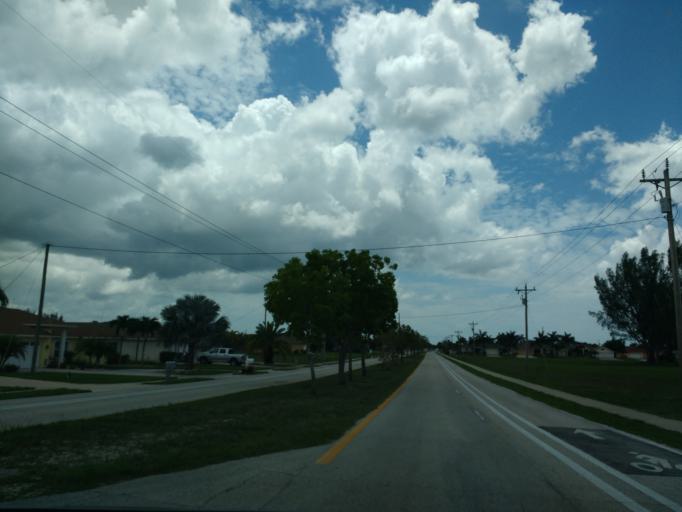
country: US
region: Florida
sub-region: Lee County
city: Cape Coral
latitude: 26.5671
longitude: -82.0174
